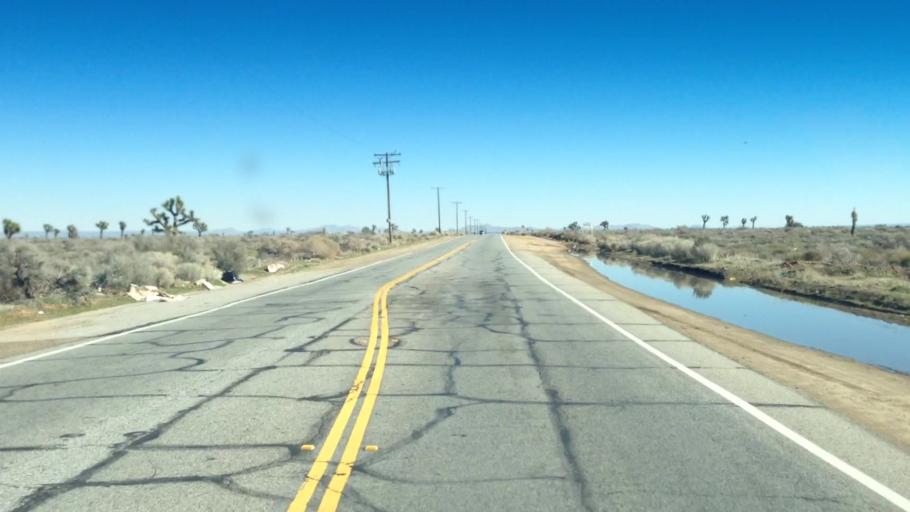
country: US
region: California
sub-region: Los Angeles County
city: Desert View Highlands
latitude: 34.6312
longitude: -118.1465
